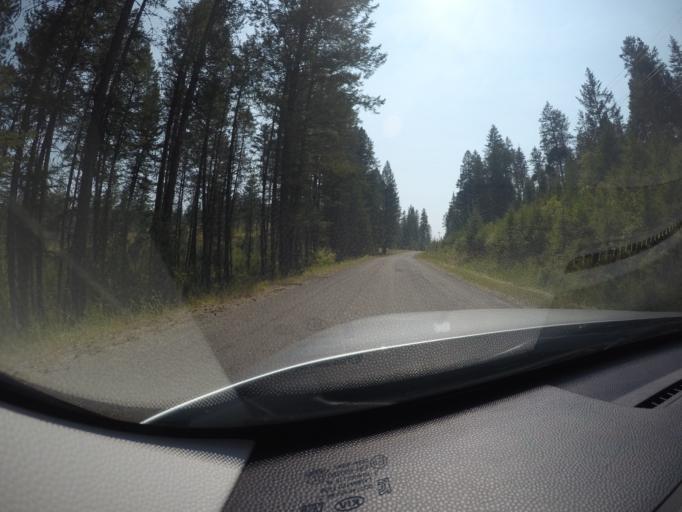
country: US
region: Montana
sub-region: Lake County
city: Polson
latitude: 47.7824
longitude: -114.1732
